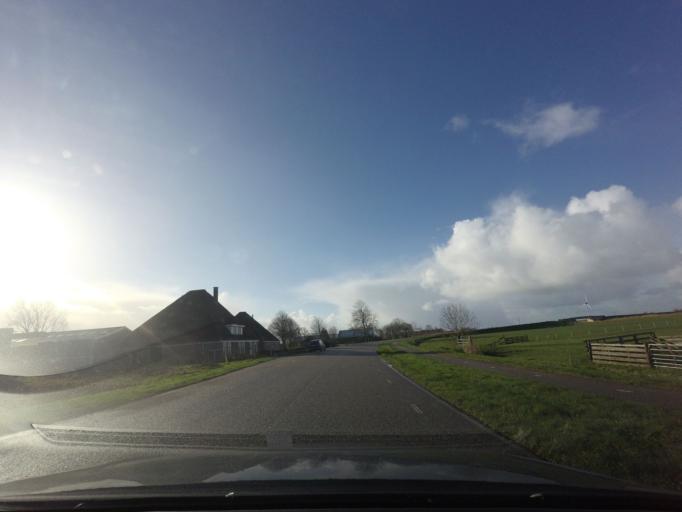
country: NL
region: North Holland
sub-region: Gemeente Heerhugowaard
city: Heerhugowaard
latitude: 52.7279
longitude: 4.8755
